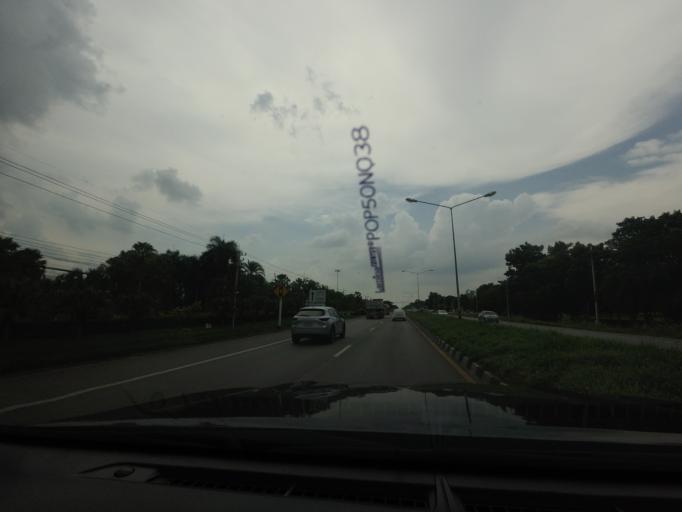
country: TH
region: Nakhon Pathom
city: Kamphaeng Saen
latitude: 14.0082
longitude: 99.9722
